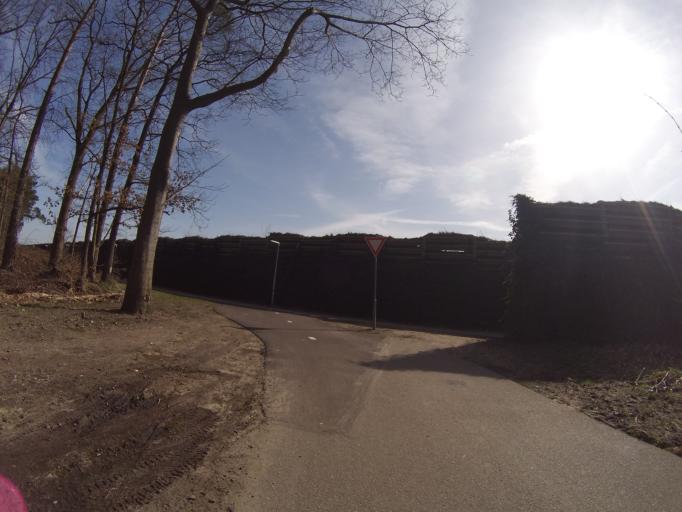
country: NL
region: Utrecht
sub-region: Gemeente Zeist
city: Zeist
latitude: 52.1103
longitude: 5.2743
